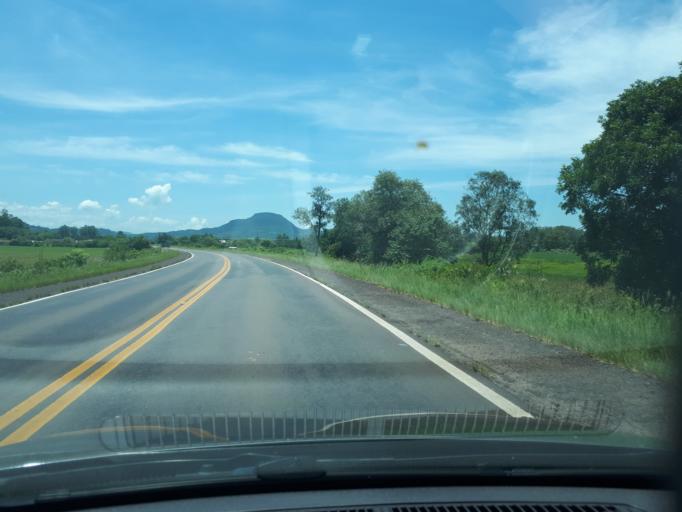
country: BR
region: Rio Grande do Sul
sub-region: Candelaria
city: Candelaria
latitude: -29.7246
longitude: -52.9224
